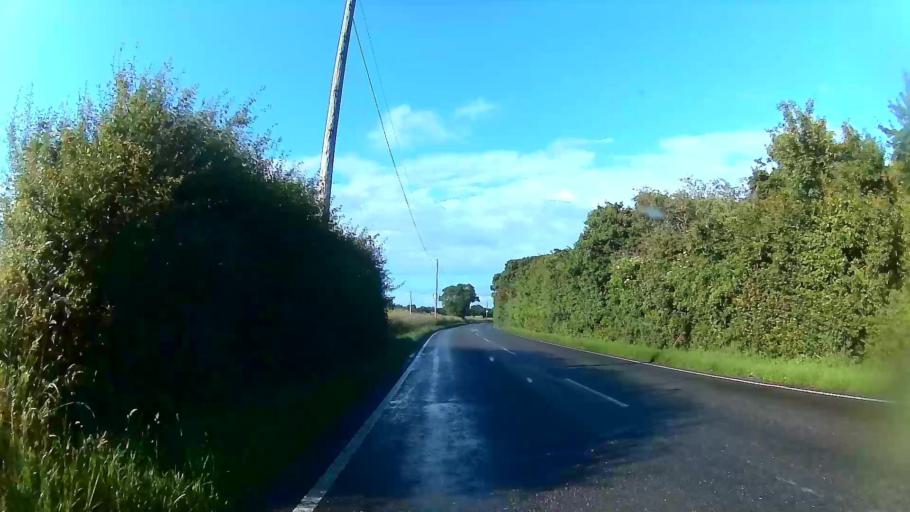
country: GB
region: England
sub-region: Essex
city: Writtle
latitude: 51.7207
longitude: 0.4010
